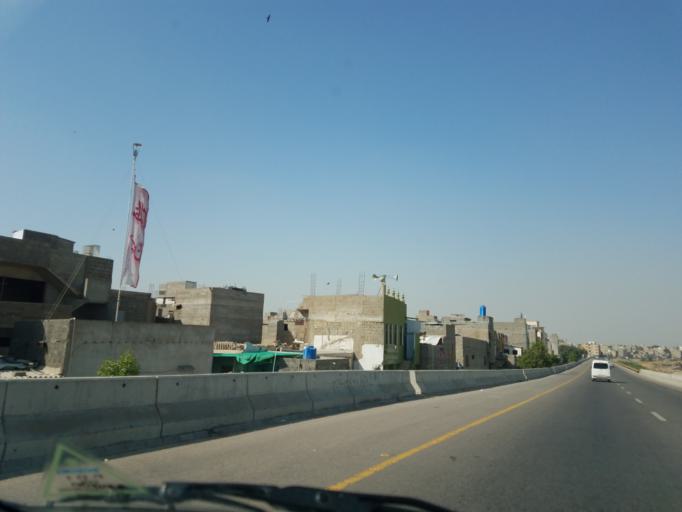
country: PK
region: Sindh
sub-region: Karachi District
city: Karachi
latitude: 24.9181
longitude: 67.0785
